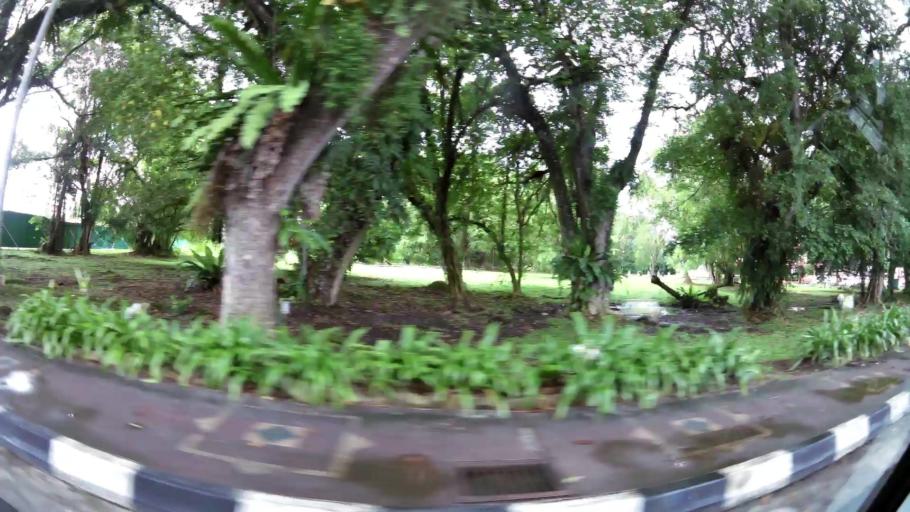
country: BN
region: Brunei and Muara
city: Bandar Seri Begawan
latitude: 4.8948
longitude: 114.9364
